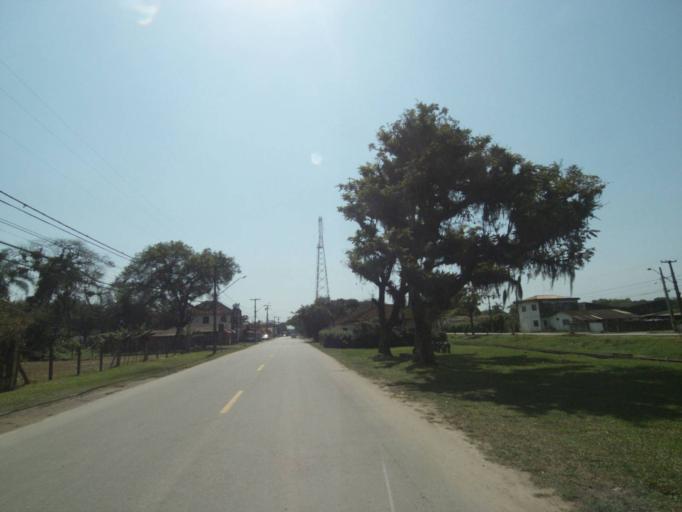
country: BR
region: Parana
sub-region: Paranagua
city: Paranagua
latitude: -25.5565
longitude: -48.6273
